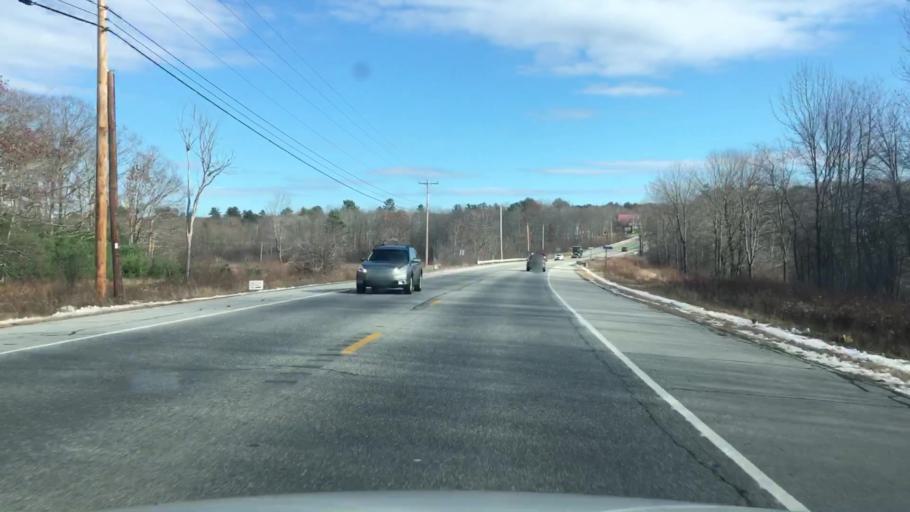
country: US
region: Maine
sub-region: Kennebec County
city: Winthrop
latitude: 44.3187
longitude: -69.9340
